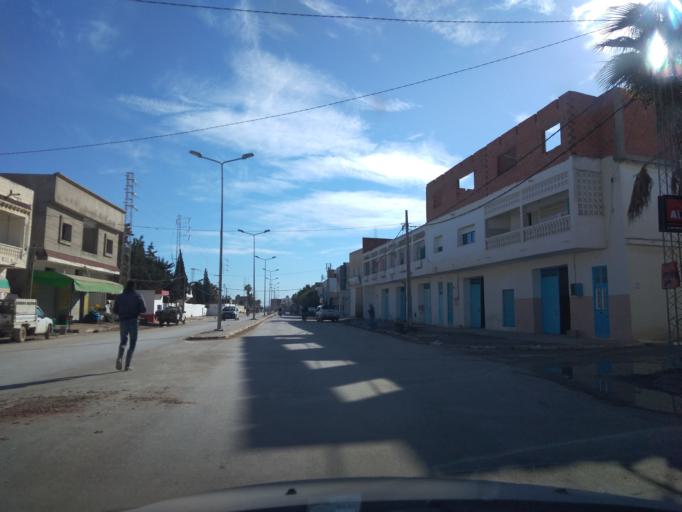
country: TN
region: Ariana
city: Qal'at al Andalus
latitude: 37.0585
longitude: 10.1198
